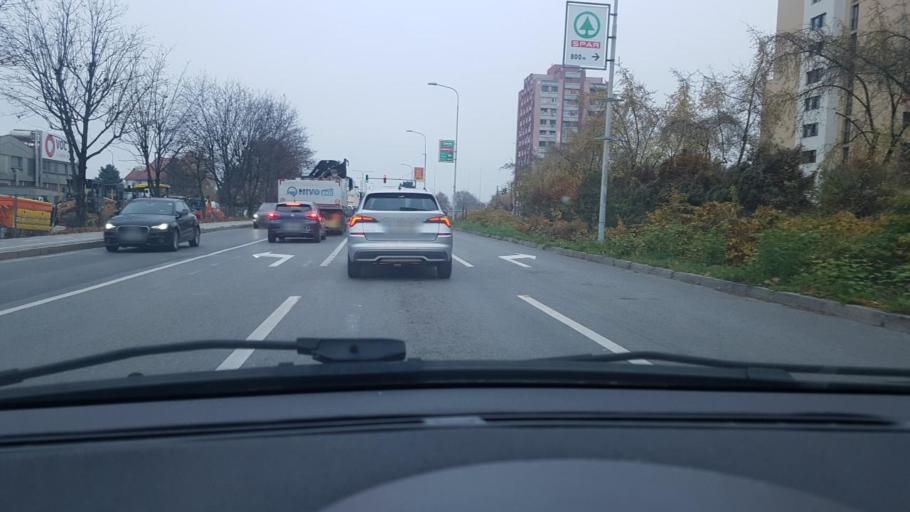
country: SI
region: Celje
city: Celje
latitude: 46.2370
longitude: 15.2522
